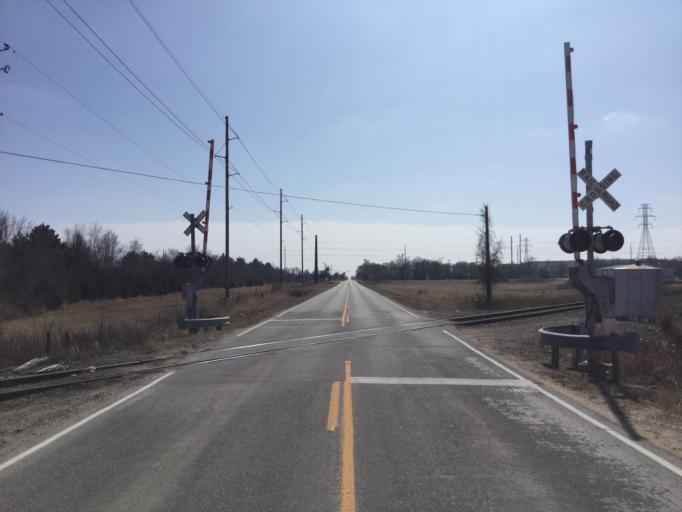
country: US
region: Kansas
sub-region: Sedgwick County
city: Haysville
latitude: 37.5962
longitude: -97.4072
